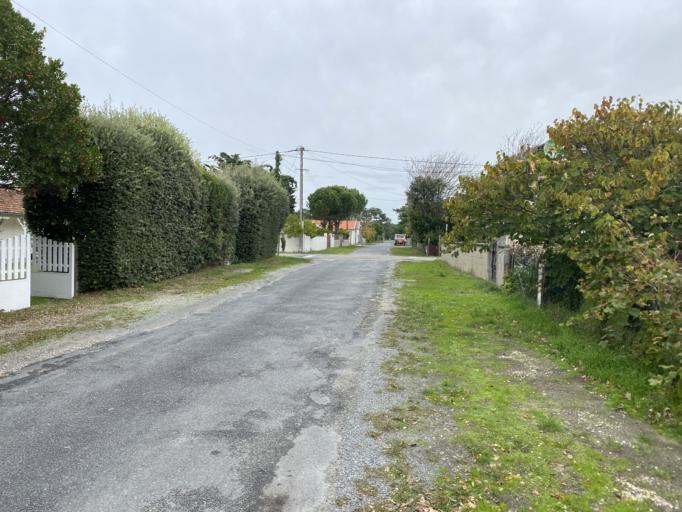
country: FR
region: Aquitaine
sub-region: Departement de la Gironde
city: Soulac-sur-Mer
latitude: 45.3787
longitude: -1.1505
